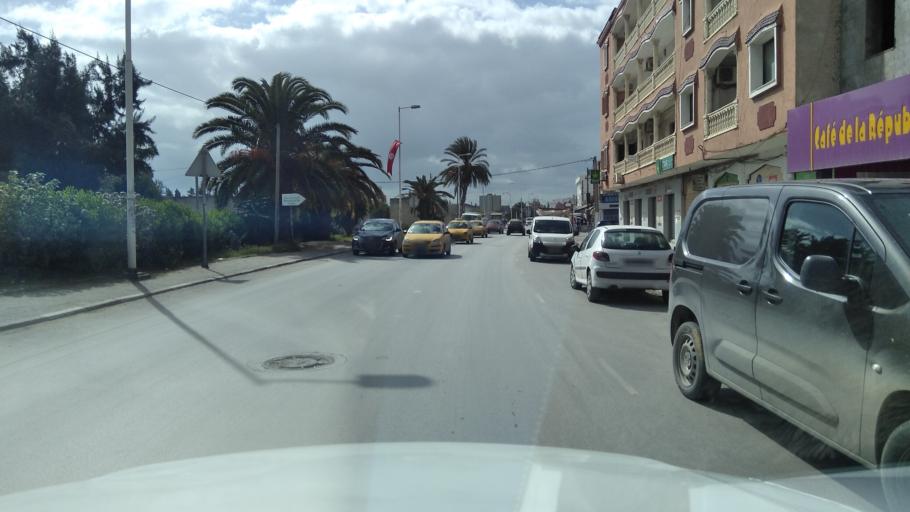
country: TN
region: Bin 'Arus
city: Ben Arous
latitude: 36.7478
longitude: 10.2256
